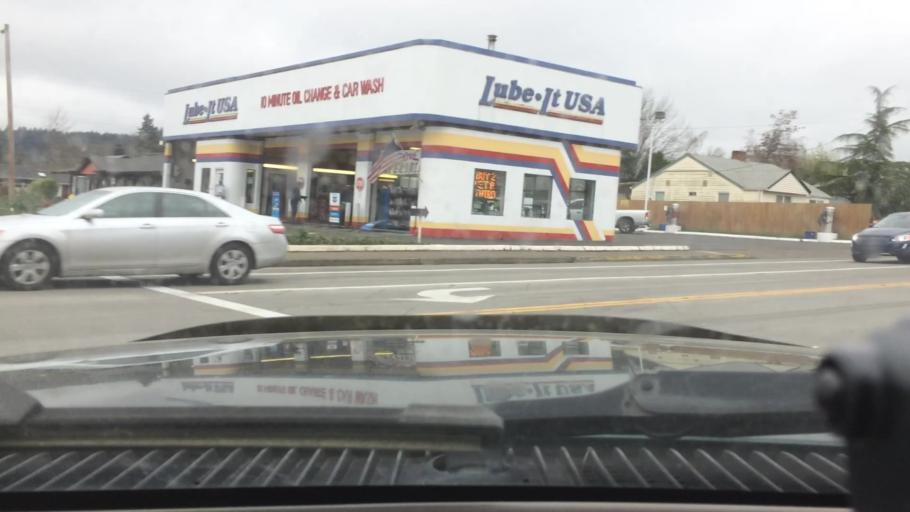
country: US
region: Oregon
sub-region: Lane County
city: Eugene
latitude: 44.0262
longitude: -123.0908
